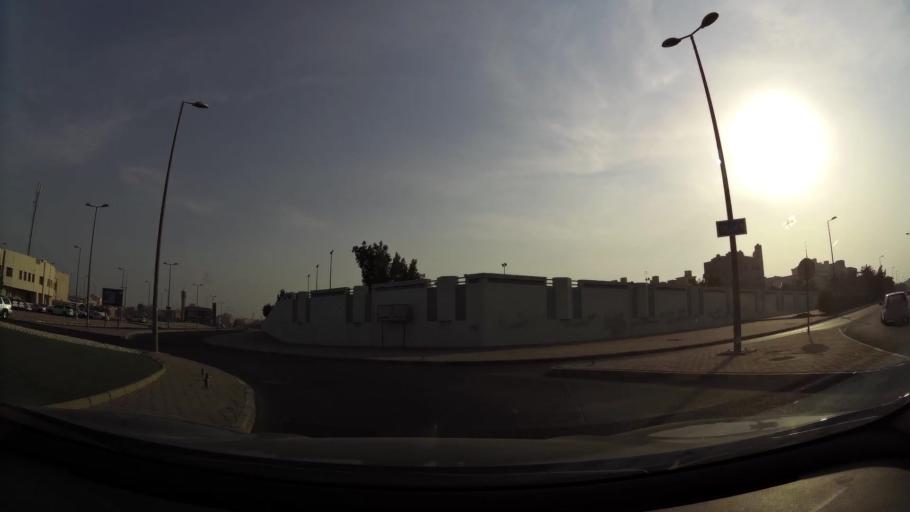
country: KW
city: Al Funaytis
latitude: 29.2383
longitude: 48.0775
